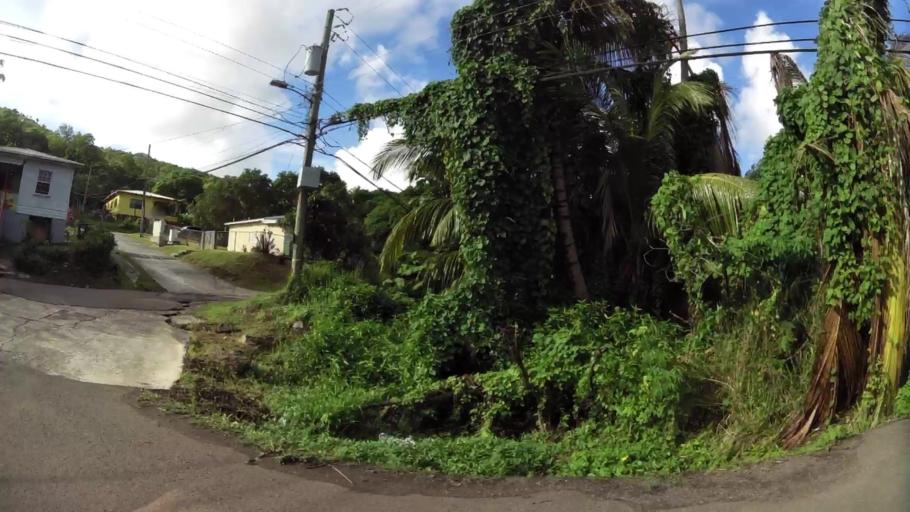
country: AG
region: Saint Peter
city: All Saints
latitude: 17.0436
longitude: -61.8217
